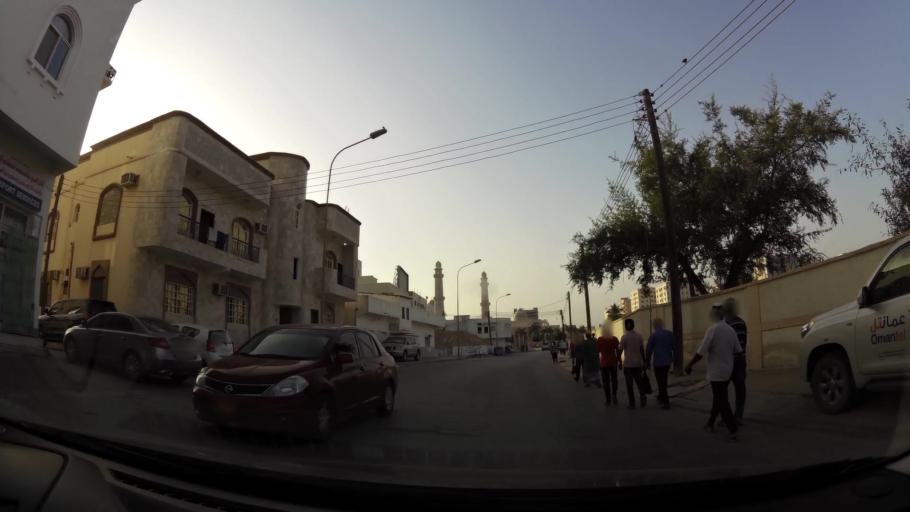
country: OM
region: Zufar
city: Salalah
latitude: 17.0145
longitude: 54.0948
